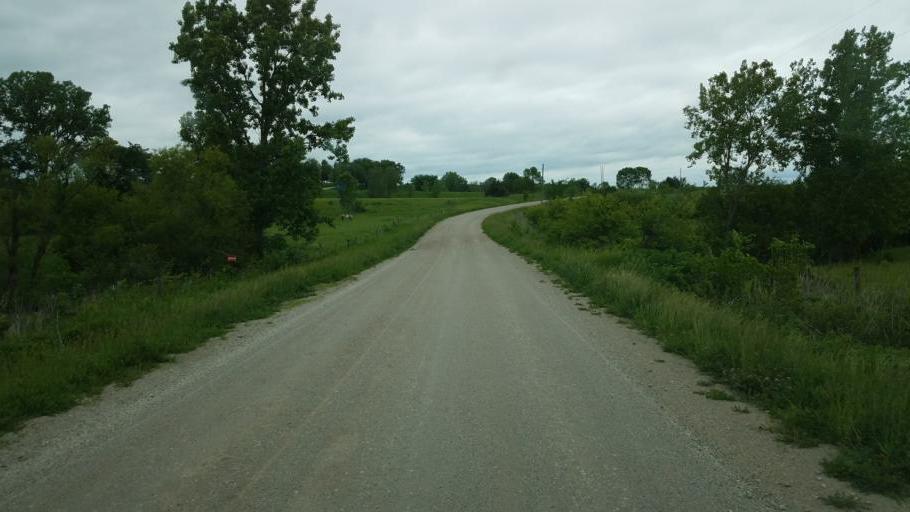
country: US
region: Iowa
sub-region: Decatur County
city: Lamoni
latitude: 40.6473
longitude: -93.8626
